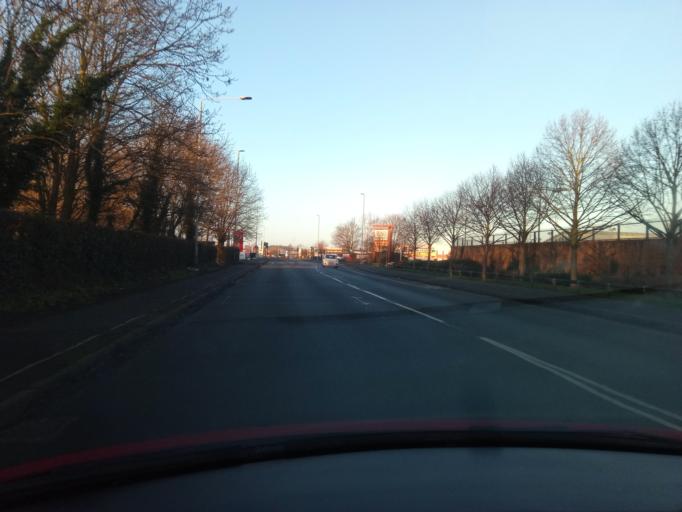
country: GB
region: England
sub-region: Leicestershire
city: Loughborough
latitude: 52.7789
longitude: -1.2077
